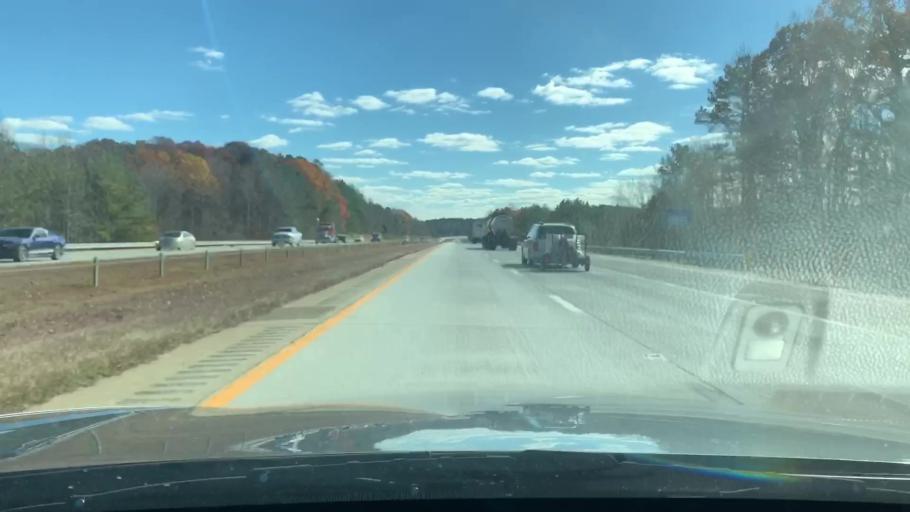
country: US
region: North Carolina
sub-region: Orange County
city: Hillsborough
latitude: 36.0054
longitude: -79.0818
